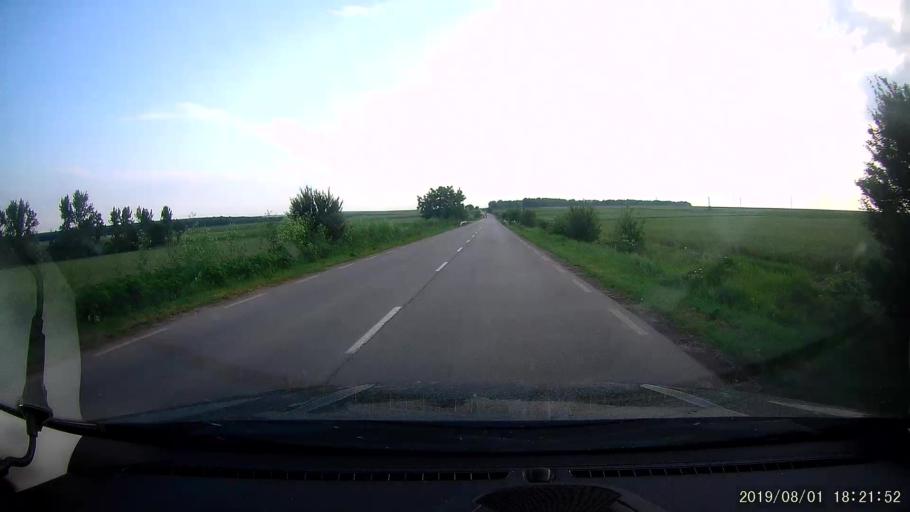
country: BG
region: Shumen
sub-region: Obshtina Kaolinovo
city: Kaolinovo
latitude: 43.6461
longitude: 27.0638
